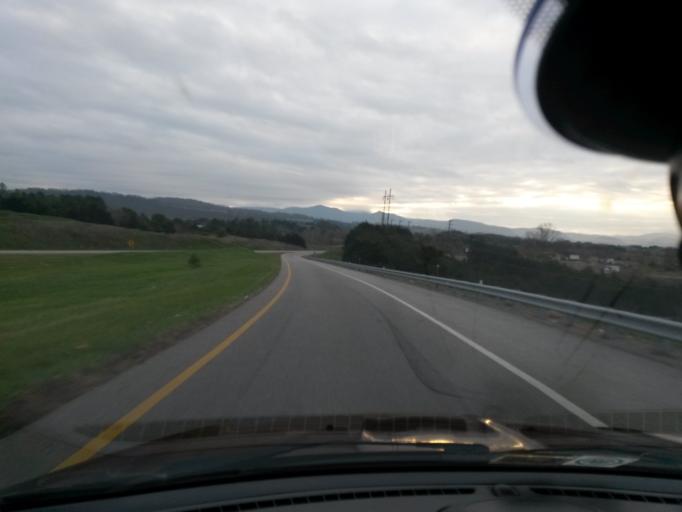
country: US
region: Virginia
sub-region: Rockbridge County
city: East Lexington
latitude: 37.8000
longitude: -79.4149
